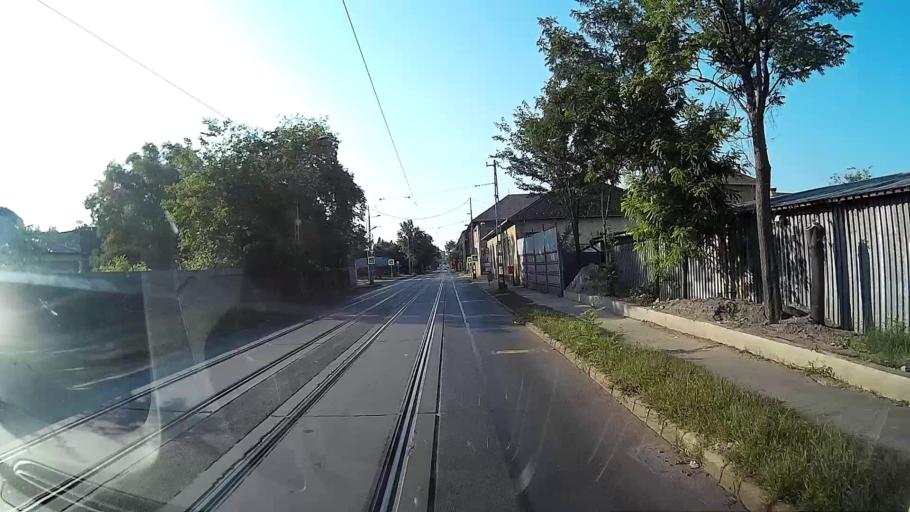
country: HU
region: Budapest
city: Budapest XX. keruelet
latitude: 47.4526
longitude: 19.0917
